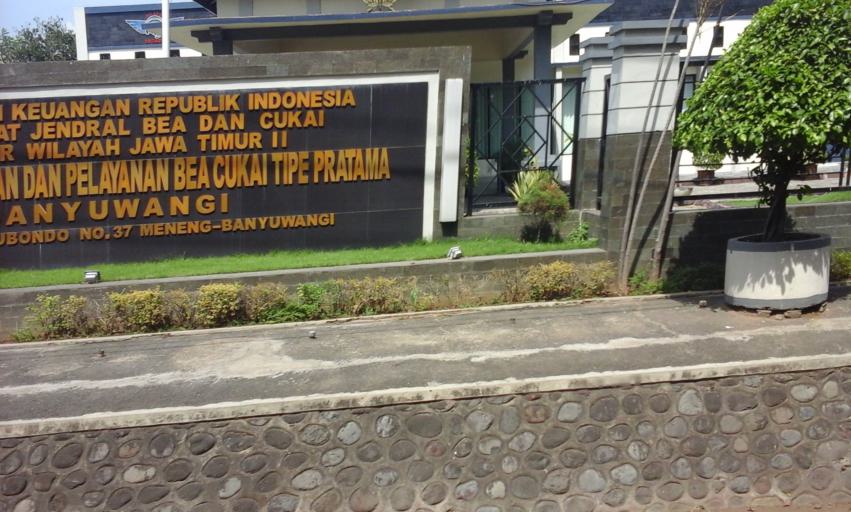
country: ID
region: East Java
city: Klatakan
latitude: -8.1361
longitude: 114.3991
